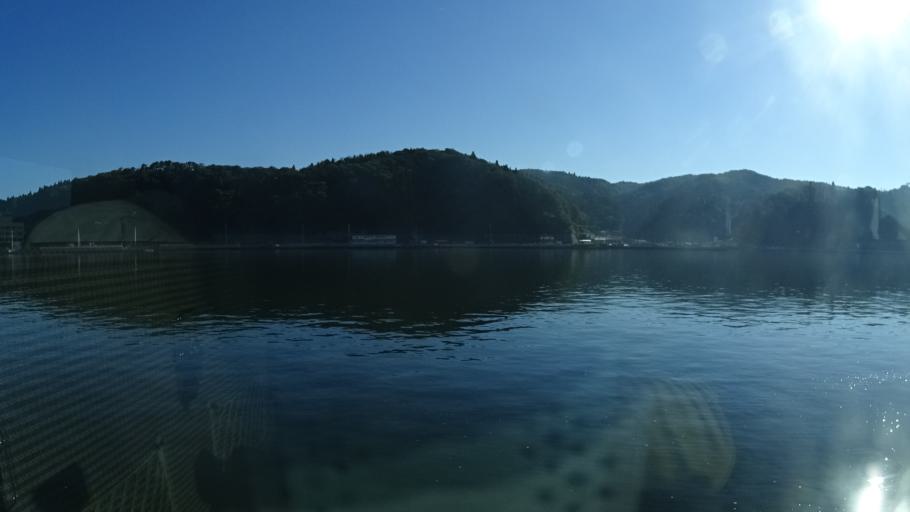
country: JP
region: Iwate
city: Ofunato
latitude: 38.8915
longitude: 141.5927
